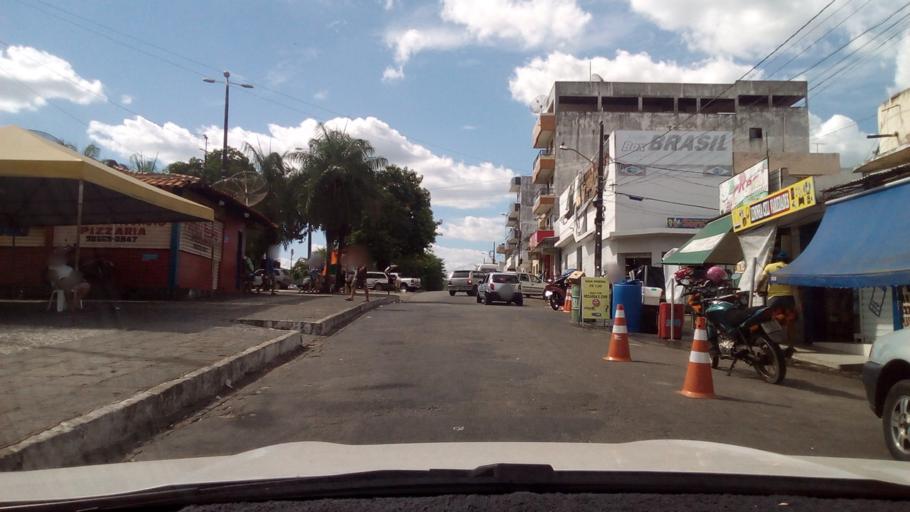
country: BR
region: Paraiba
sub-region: Guarabira
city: Guarabira
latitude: -6.8509
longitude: -35.4926
